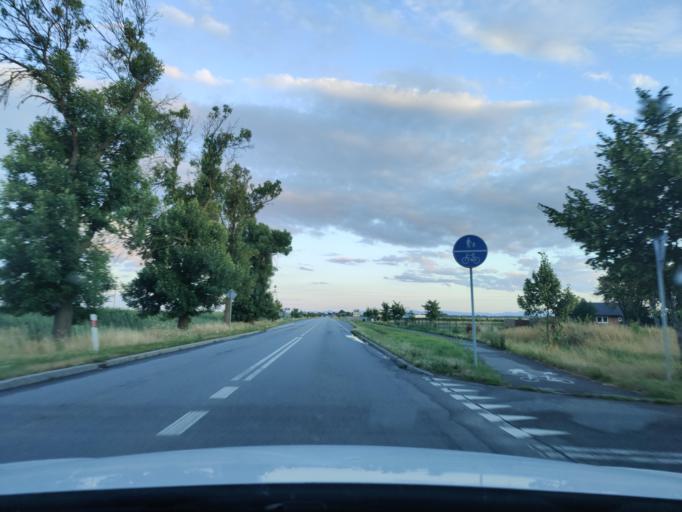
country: PL
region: Opole Voivodeship
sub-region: Powiat brzeski
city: Grodkow
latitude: 50.6737
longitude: 17.3879
